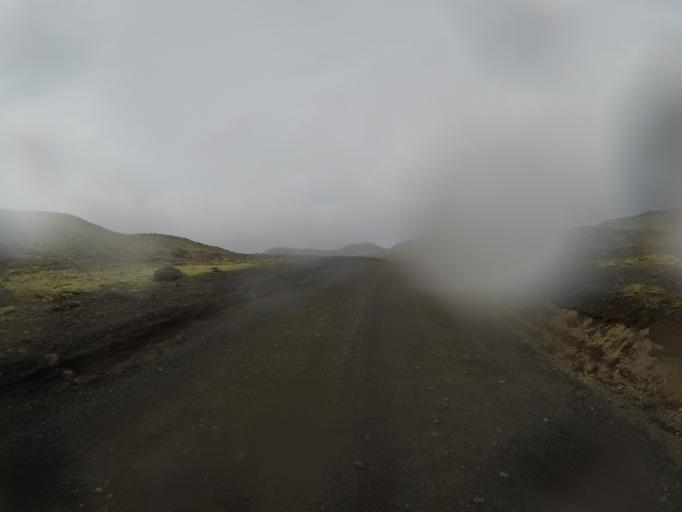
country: IS
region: South
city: Vestmannaeyjar
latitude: 63.9810
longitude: -18.8488
